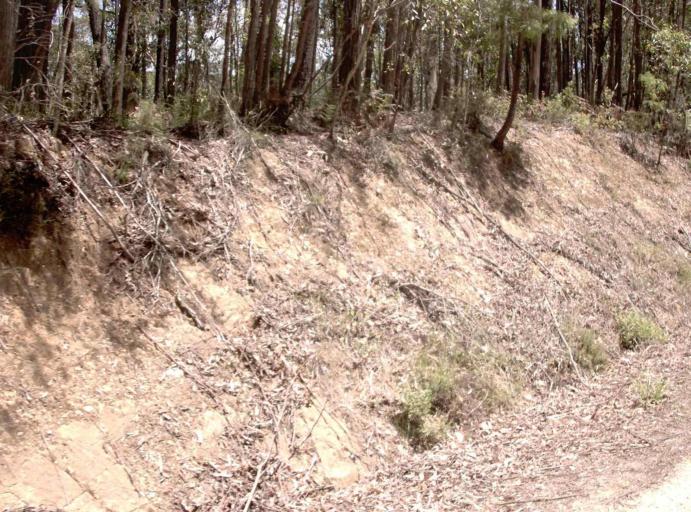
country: AU
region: New South Wales
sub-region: Bombala
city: Bombala
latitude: -37.5814
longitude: 148.9418
